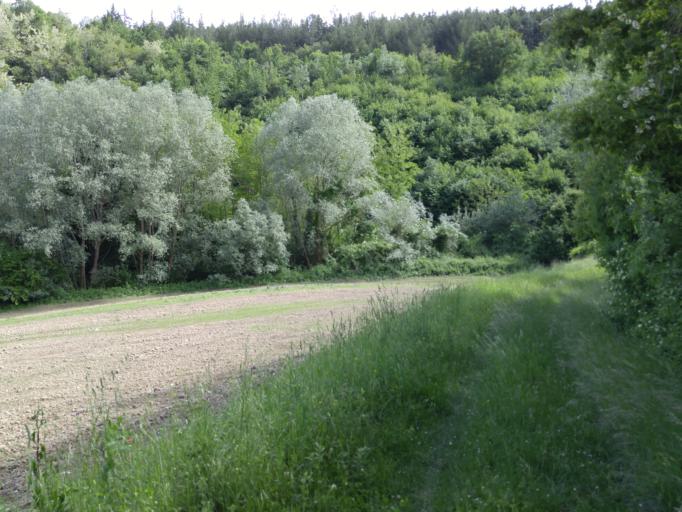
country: IT
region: The Marches
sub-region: Provincia di Pesaro e Urbino
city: Fermignano
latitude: 43.6957
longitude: 12.6215
